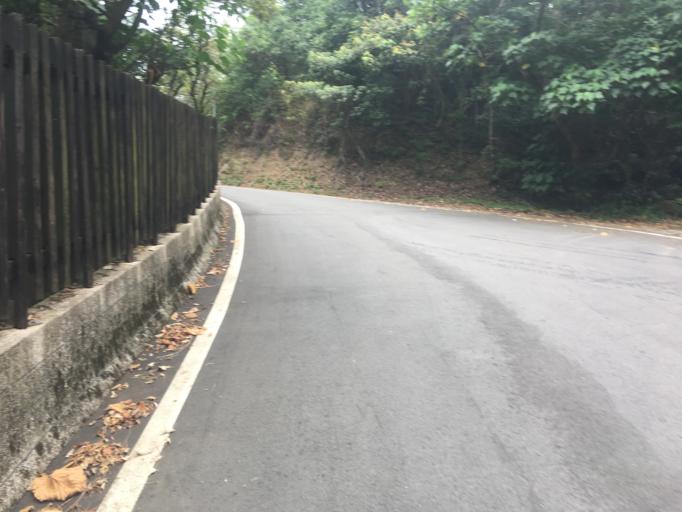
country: TW
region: Taipei
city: Taipei
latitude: 25.0882
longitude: 121.5543
